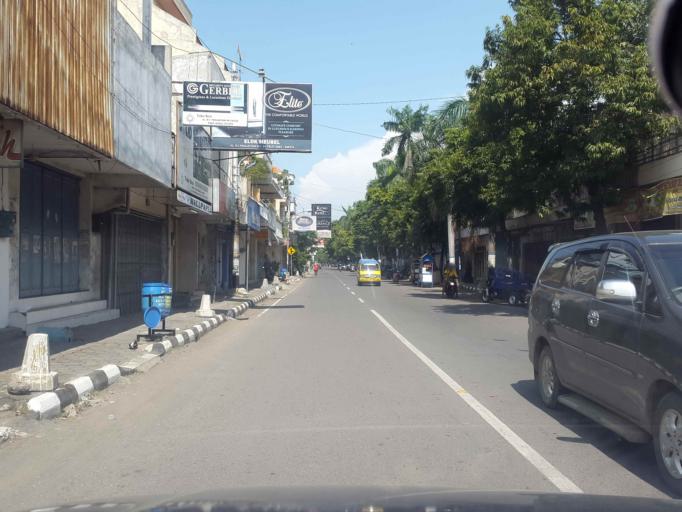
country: ID
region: Central Java
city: Tegal
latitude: -6.8594
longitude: 109.1349
